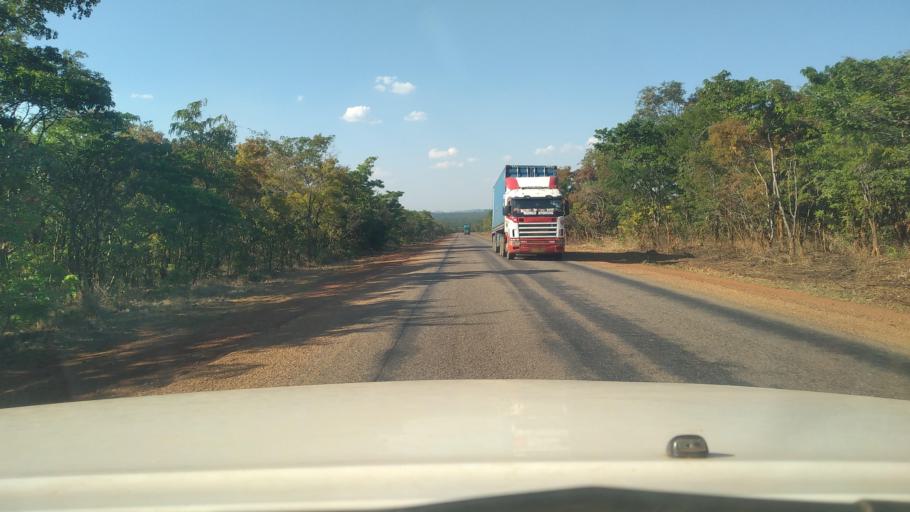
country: ZM
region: Northern
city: Mpika
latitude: -11.7566
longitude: 31.4636
